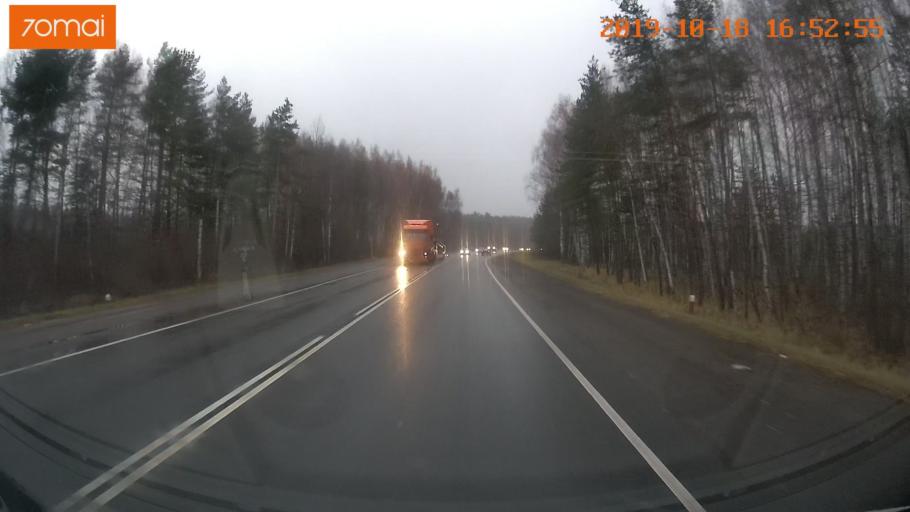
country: RU
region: Ivanovo
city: Nerl'
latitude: 56.6078
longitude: 40.5564
